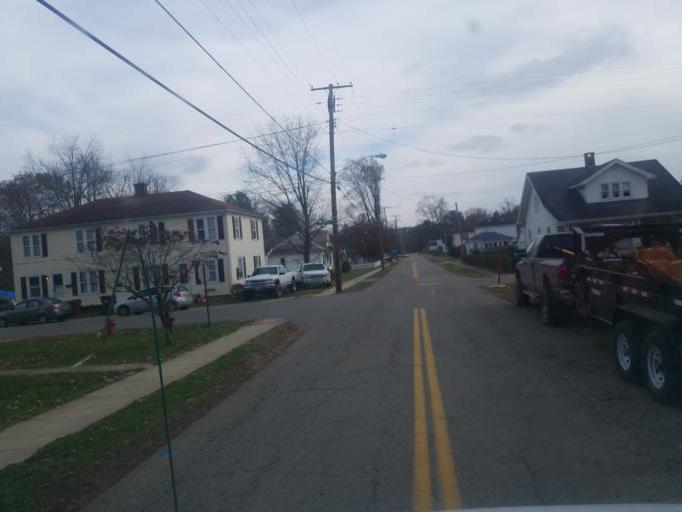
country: US
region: Ohio
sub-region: Knox County
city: Mount Vernon
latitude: 40.3978
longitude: -82.4740
